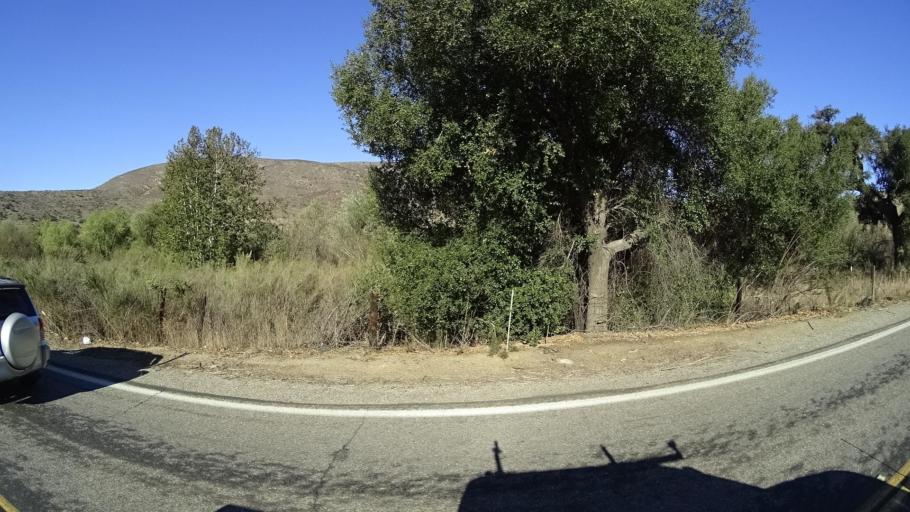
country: US
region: California
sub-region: San Diego County
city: Jamul
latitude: 32.6489
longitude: -116.8692
